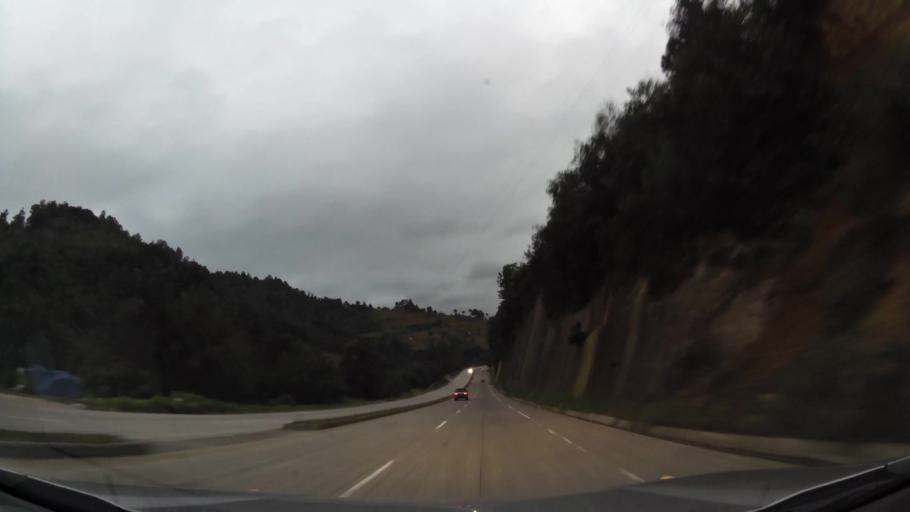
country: GT
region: Chimaltenango
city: Santa Apolonia
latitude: 14.8449
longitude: -91.0428
